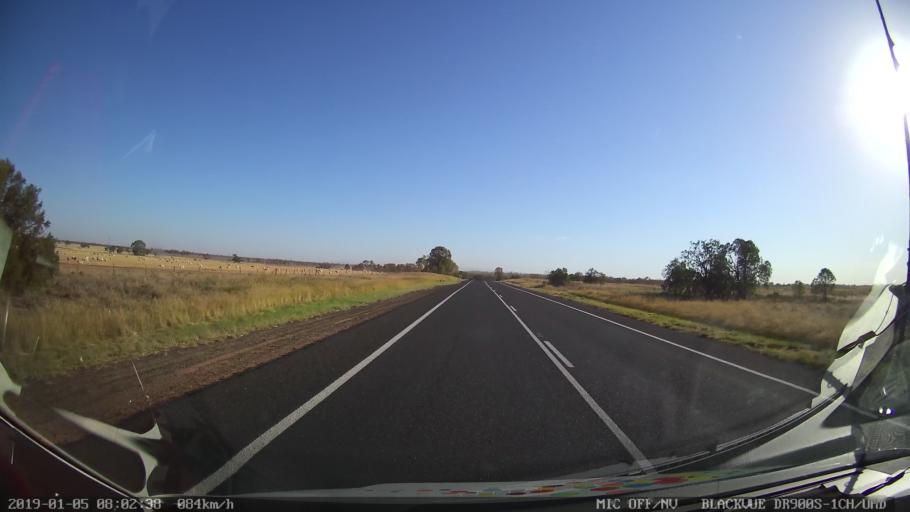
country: AU
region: New South Wales
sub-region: Gilgandra
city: Gilgandra
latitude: -31.6738
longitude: 148.7131
